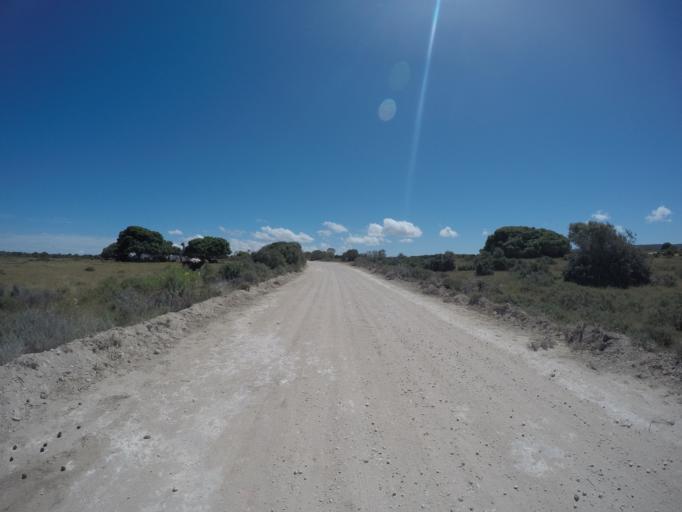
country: ZA
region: Western Cape
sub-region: Overberg District Municipality
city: Bredasdorp
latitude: -34.4557
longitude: 20.4099
